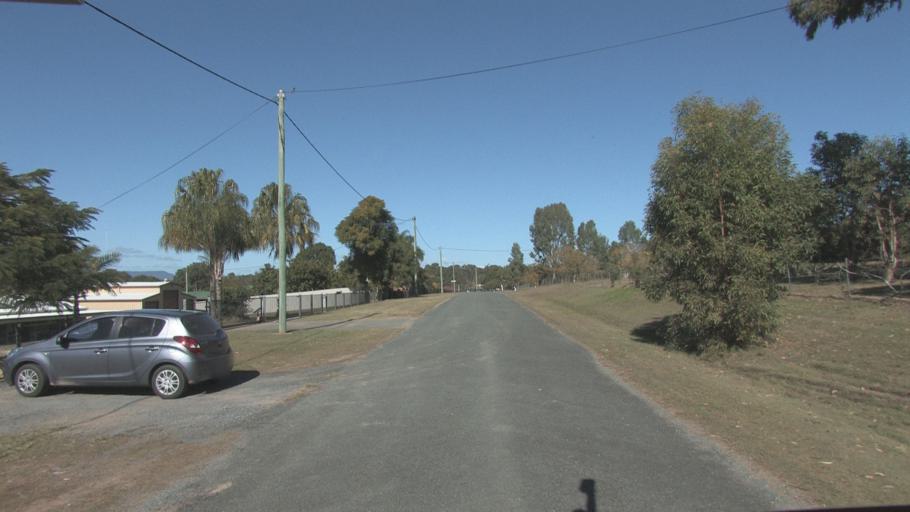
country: AU
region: Queensland
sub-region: Logan
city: Chambers Flat
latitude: -27.7598
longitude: 153.0948
